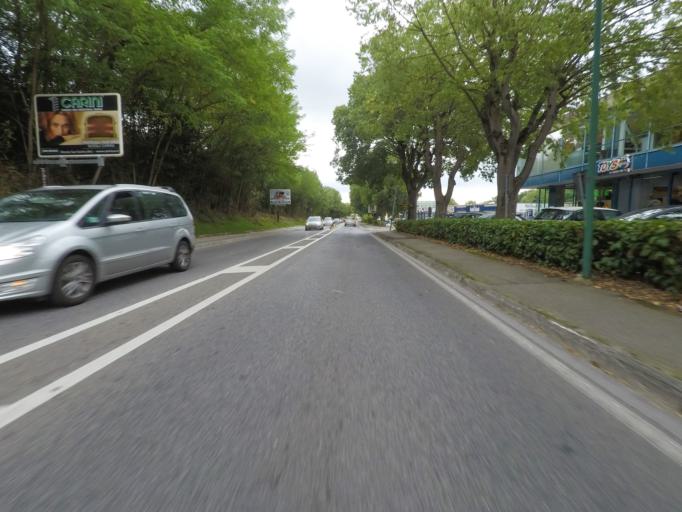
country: IT
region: Tuscany
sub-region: Provincia di Siena
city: Siena
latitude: 43.3237
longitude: 11.3456
